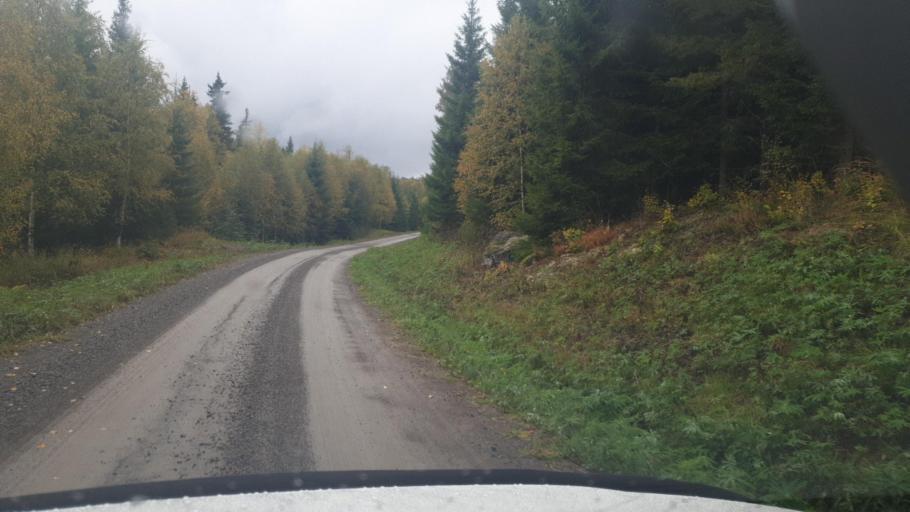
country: SE
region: Vaermland
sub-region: Sunne Kommun
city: Sunne
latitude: 59.8580
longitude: 12.8630
